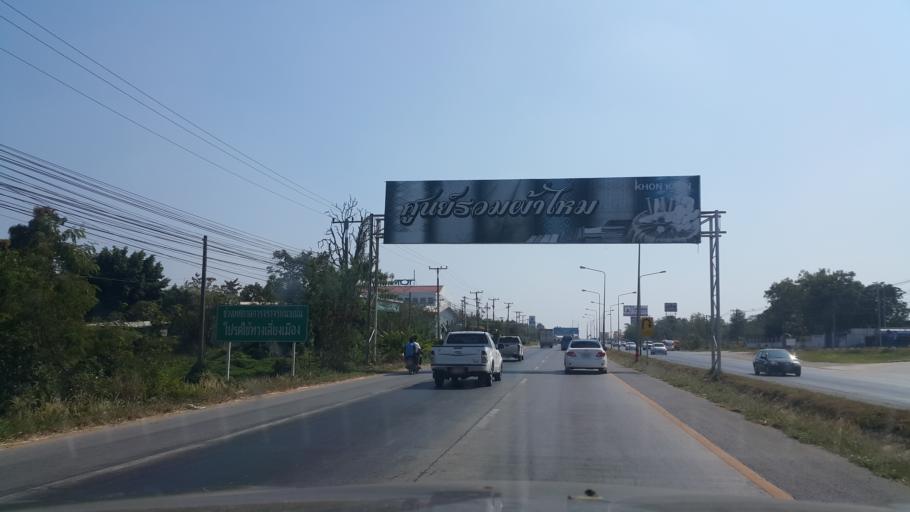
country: TH
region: Khon Kaen
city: Khon Kaen
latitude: 16.5306
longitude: 102.8304
